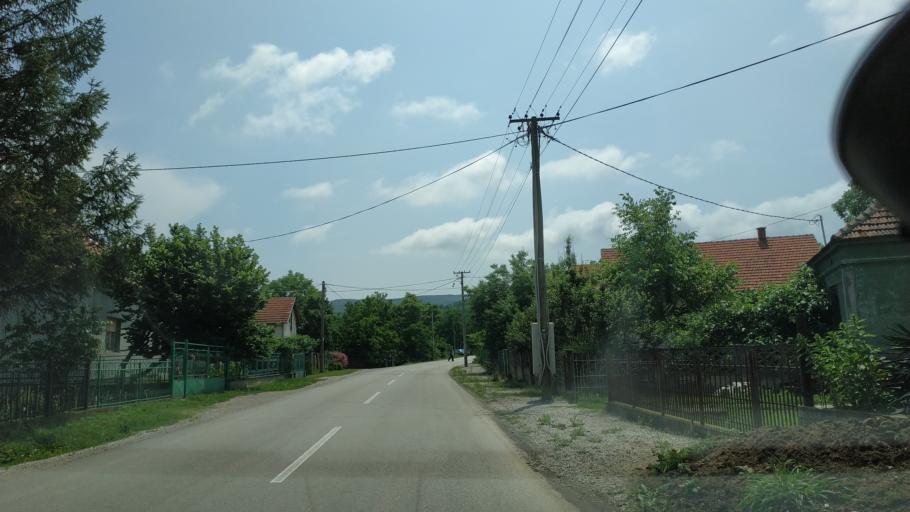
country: RS
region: Central Serbia
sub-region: Nisavski Okrug
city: Aleksinac
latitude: 43.4282
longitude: 21.7437
